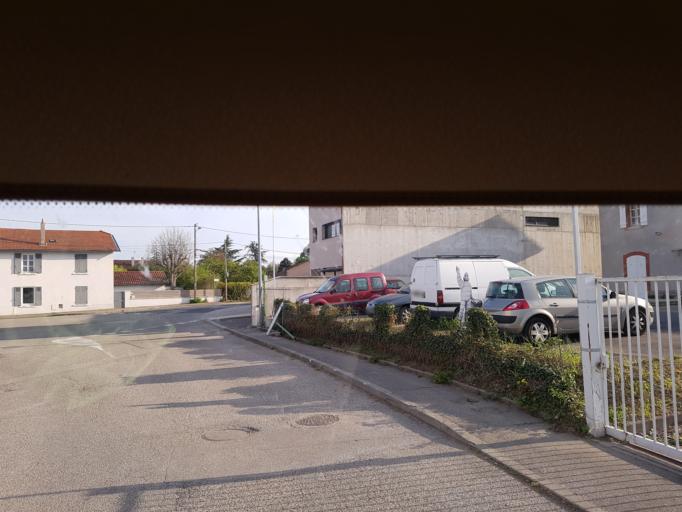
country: FR
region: Rhone-Alpes
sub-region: Departement du Rhone
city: Messimy
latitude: 45.7009
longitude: 4.6918
